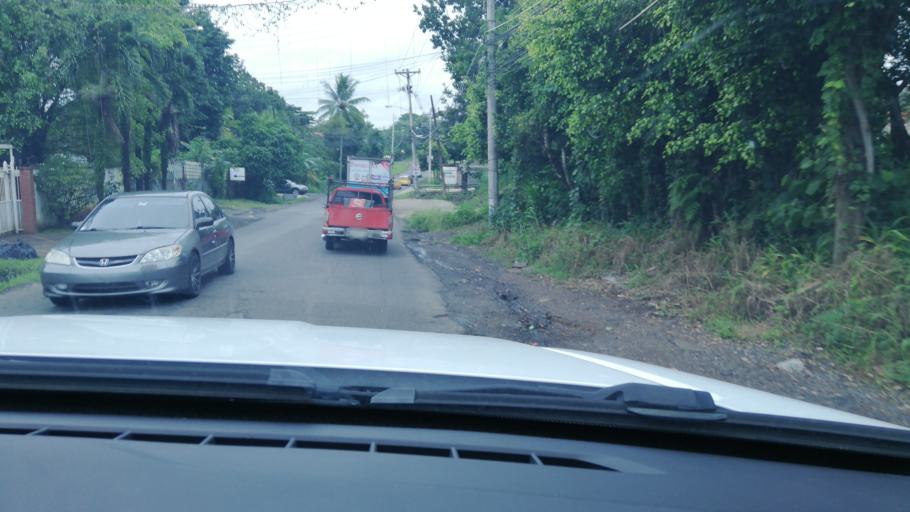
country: PA
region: Panama
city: Las Cumbres
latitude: 9.0756
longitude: -79.5212
